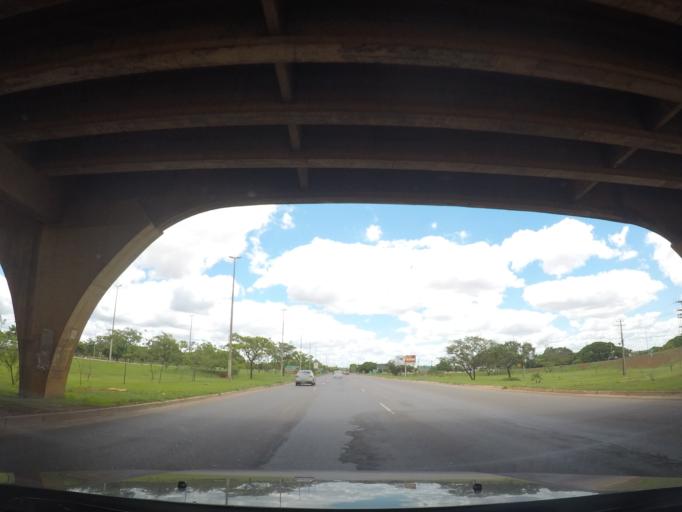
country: BR
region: Federal District
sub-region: Brasilia
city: Brasilia
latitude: -15.7745
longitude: -47.9378
